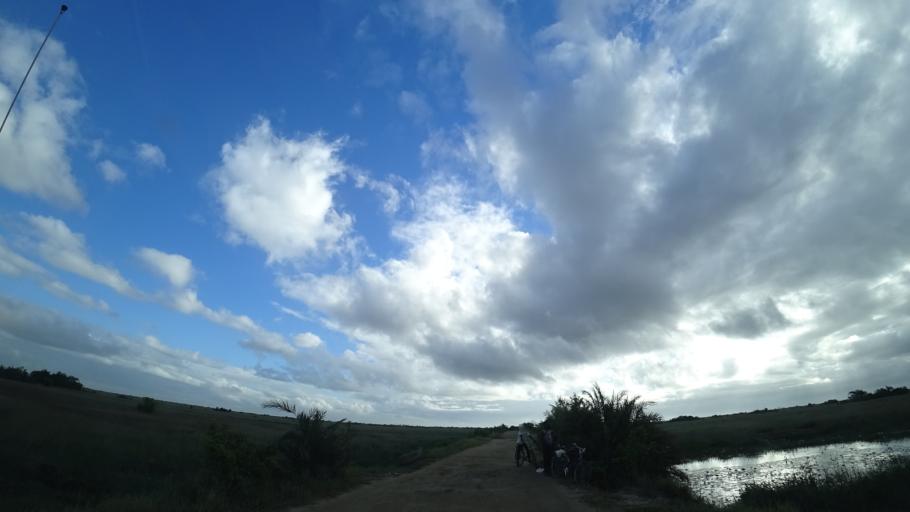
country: MZ
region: Sofala
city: Beira
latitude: -19.7090
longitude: 35.0172
